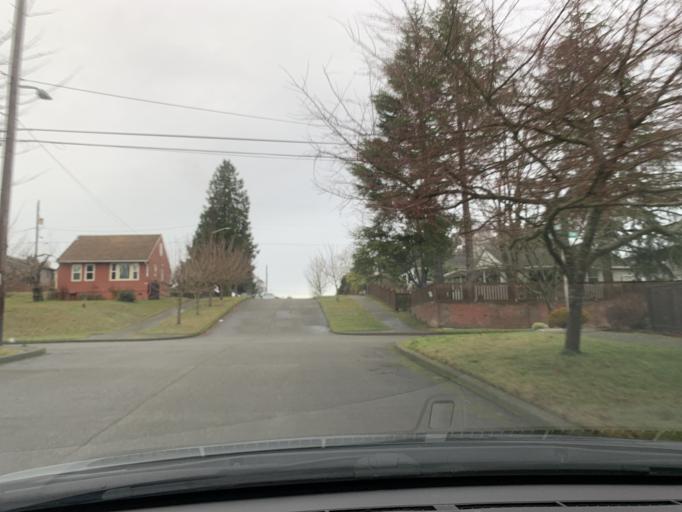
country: US
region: Washington
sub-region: King County
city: White Center
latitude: 47.5302
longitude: -122.3575
